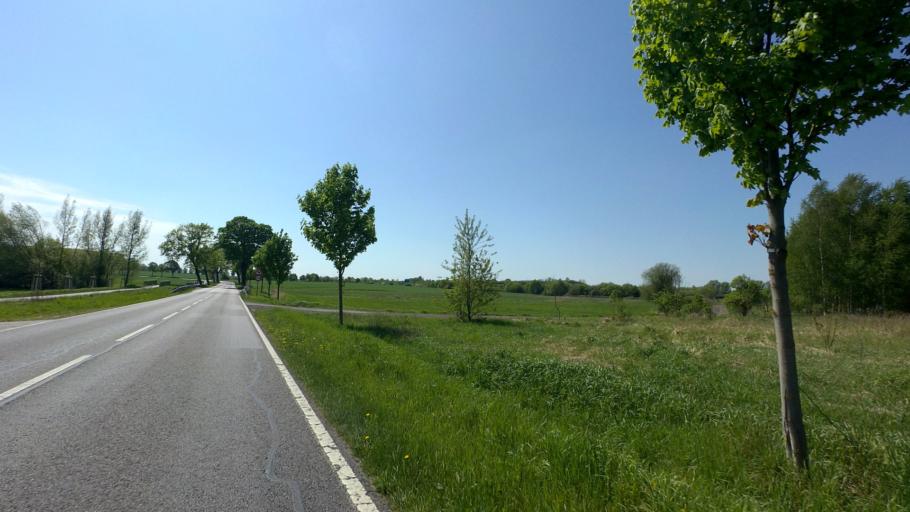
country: DE
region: Brandenburg
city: Schulzendorf
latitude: 52.3519
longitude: 13.5576
